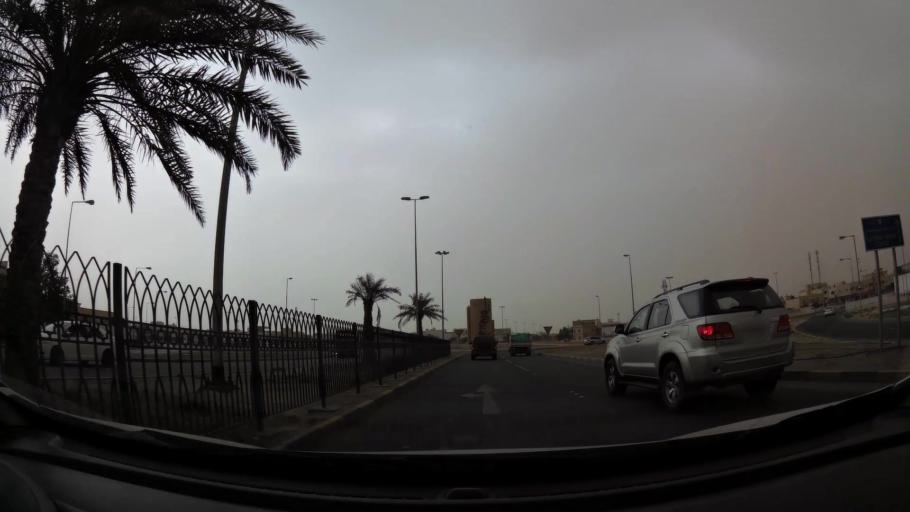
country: BH
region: Northern
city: Madinat `Isa
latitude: 26.1656
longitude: 50.5644
